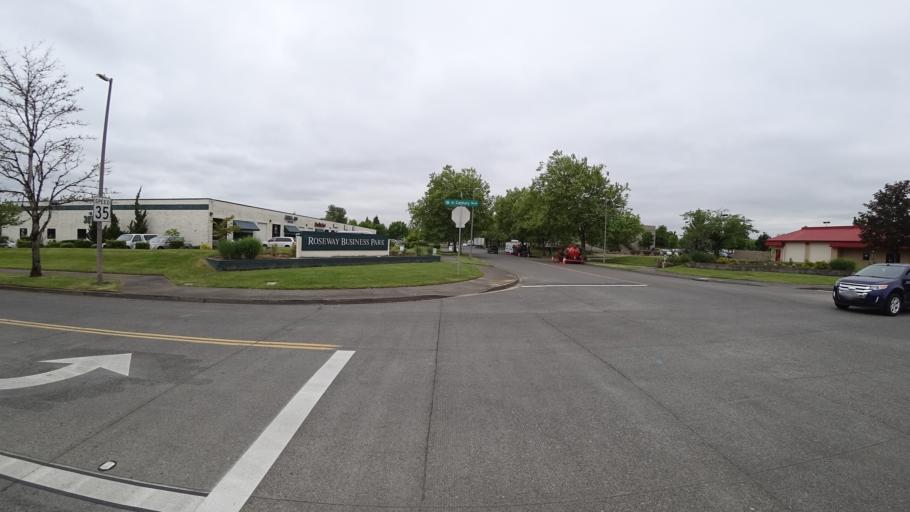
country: US
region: Oregon
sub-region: Washington County
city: Aloha
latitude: 45.4970
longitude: -122.9179
